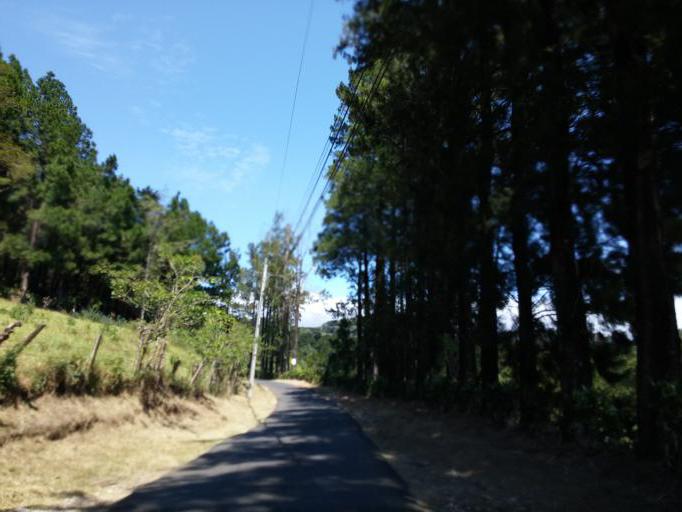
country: CR
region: Heredia
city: Santo Domingo
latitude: 10.0673
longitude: -84.1266
